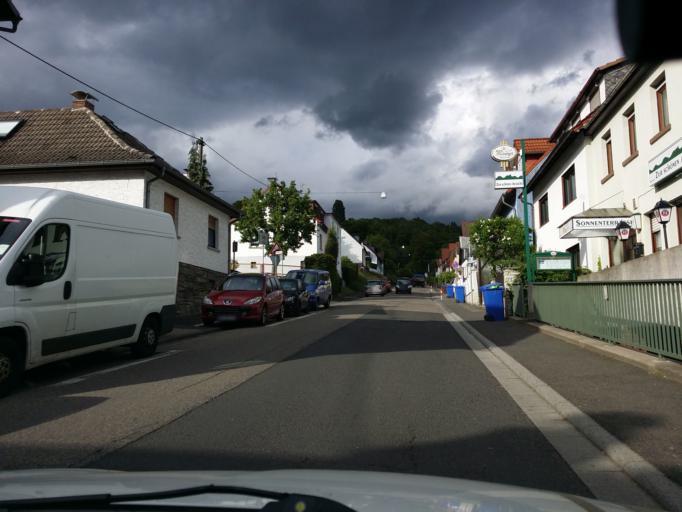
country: DE
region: Hesse
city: Eppstein
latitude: 50.1749
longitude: 8.4011
